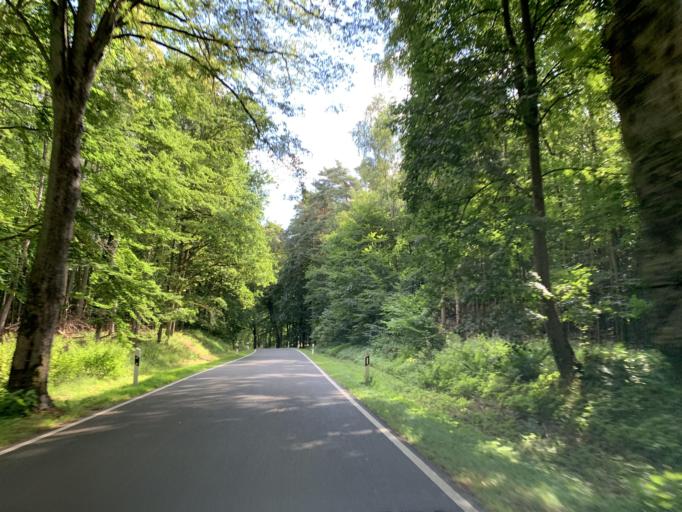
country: DE
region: Mecklenburg-Vorpommern
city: Wustrow
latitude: 53.4003
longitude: 13.1423
